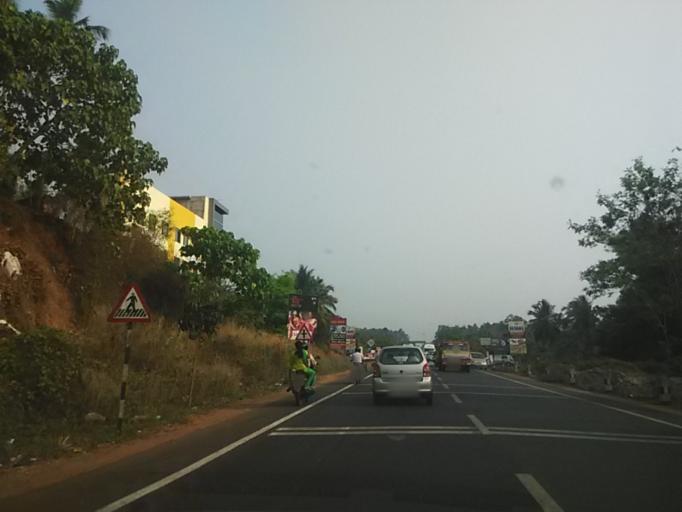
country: IN
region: Kerala
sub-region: Kozhikode
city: Kozhikode
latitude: 11.2938
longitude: 75.7978
